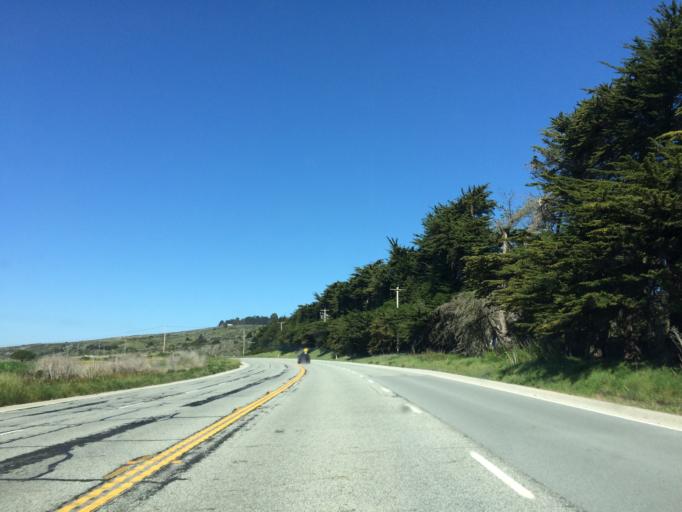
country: US
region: California
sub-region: Santa Cruz County
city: Boulder Creek
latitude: 37.1724
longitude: -122.3633
